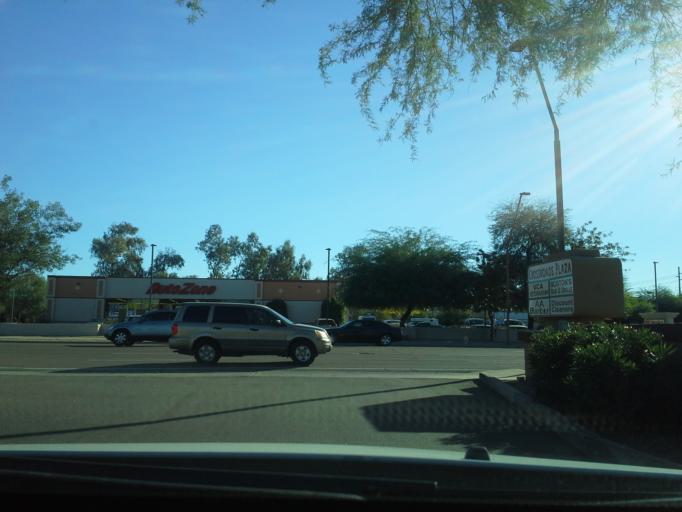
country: US
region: Arizona
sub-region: Maricopa County
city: Guadalupe
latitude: 33.3503
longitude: -111.9116
